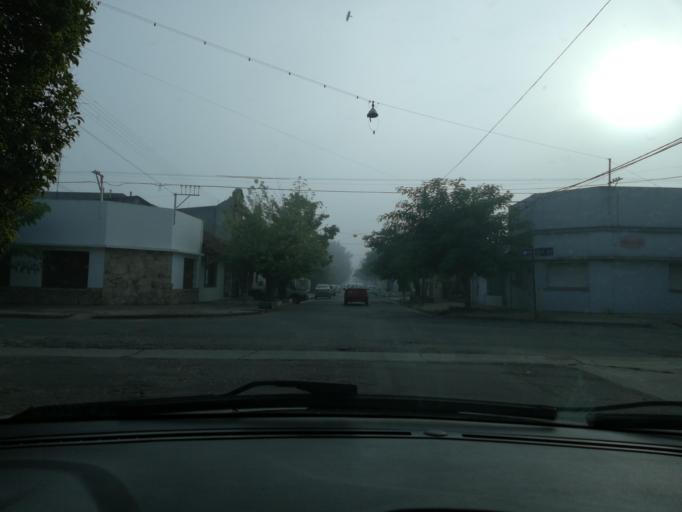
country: AR
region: Buenos Aires
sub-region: Partido de Balcarce
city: Balcarce
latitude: -37.8520
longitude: -58.2602
